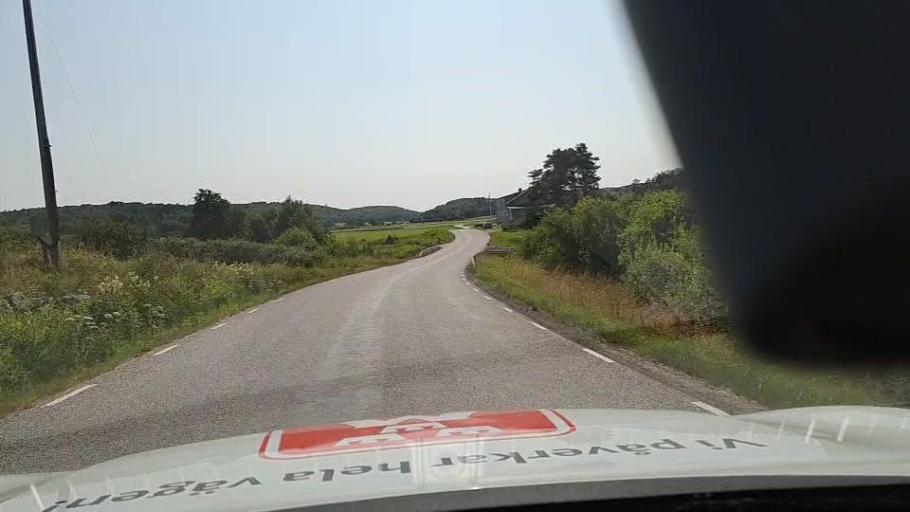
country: SE
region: Vaestra Goetaland
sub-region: Tjorns Kommun
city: Skaerhamn
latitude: 58.1292
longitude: 11.5574
